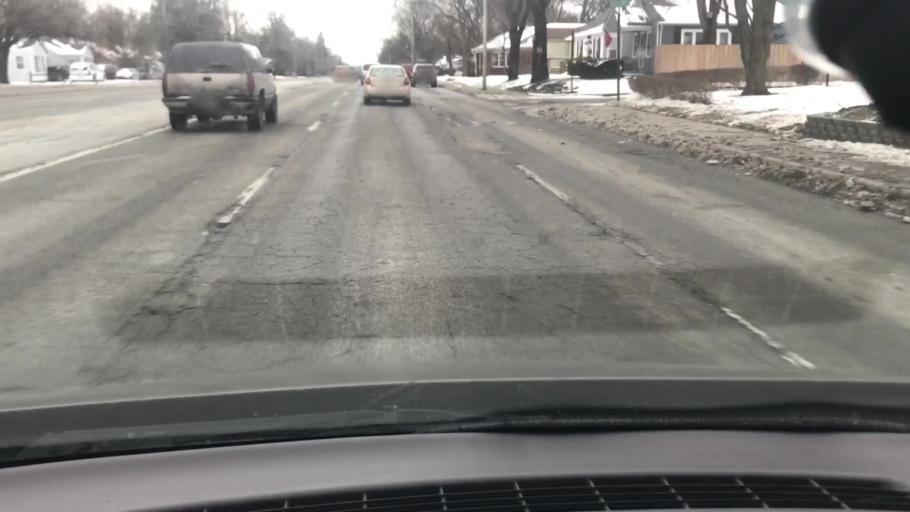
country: US
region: Indiana
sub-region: Marion County
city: Broad Ripple
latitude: 39.8564
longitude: -86.1220
